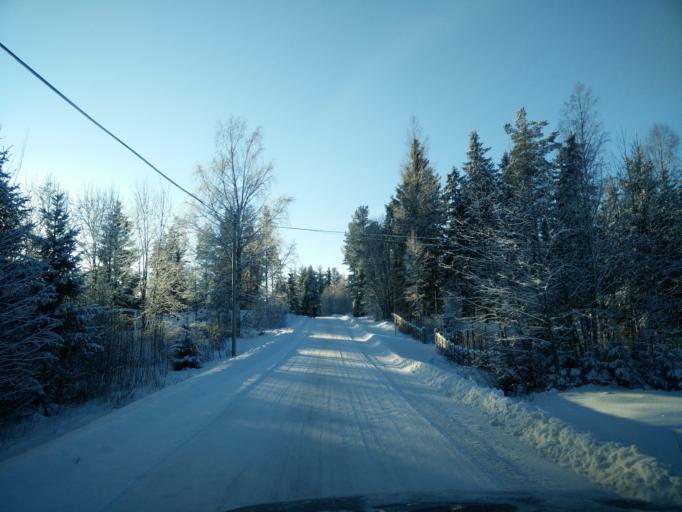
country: SE
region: Vaesternorrland
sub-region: Sundsvalls Kommun
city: Njurundabommen
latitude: 62.2290
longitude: 17.5004
